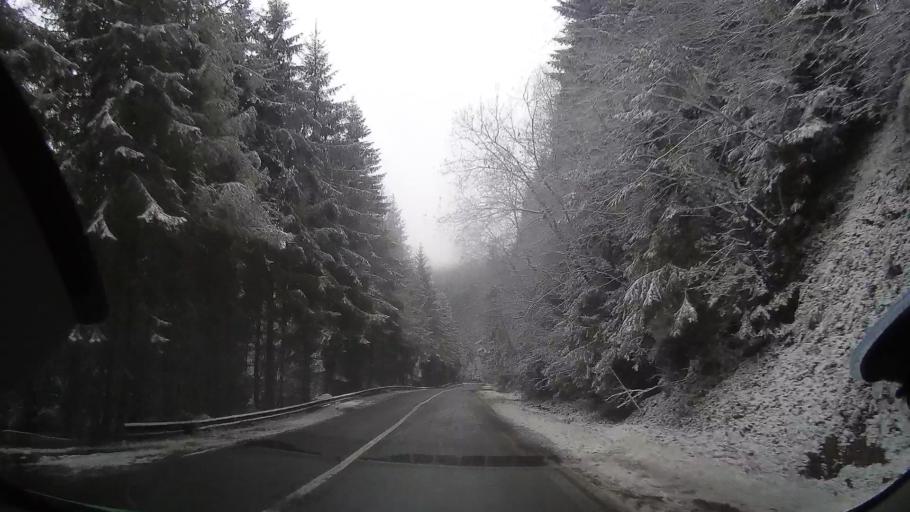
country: RO
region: Cluj
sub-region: Comuna Belis
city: Belis
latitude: 46.6501
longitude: 23.0495
